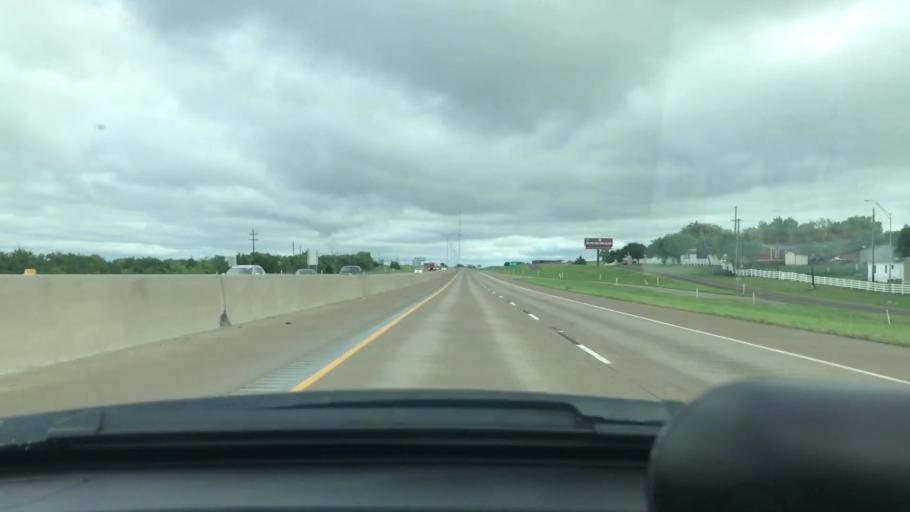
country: US
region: Texas
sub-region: Grayson County
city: Howe
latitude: 33.5127
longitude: -96.6166
